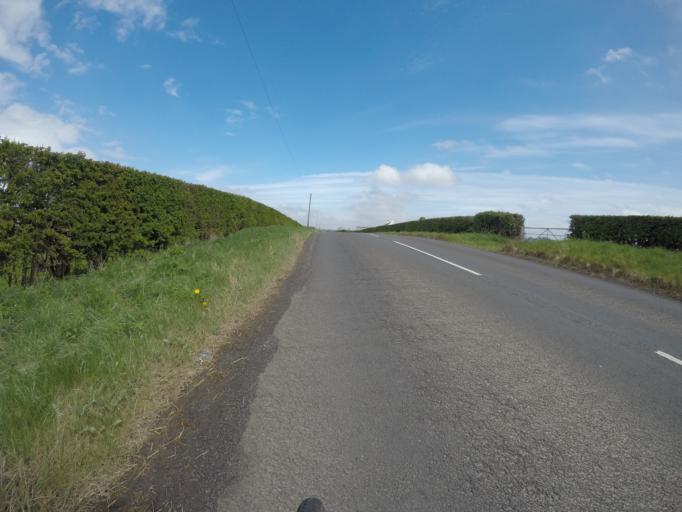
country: GB
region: Scotland
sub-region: East Ayrshire
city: Kilmaurs
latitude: 55.6546
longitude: -4.5601
